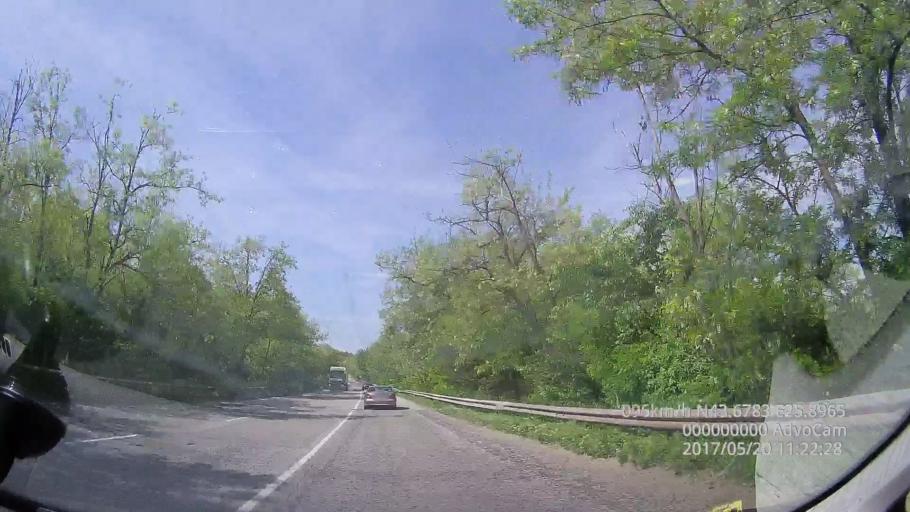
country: BG
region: Ruse
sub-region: Obshtina Dve Mogili
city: Dve Mogili
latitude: 43.6782
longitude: 25.8963
